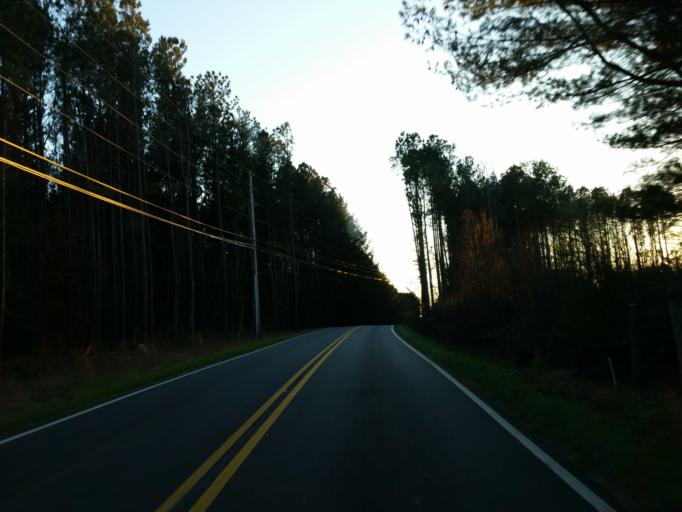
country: US
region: Georgia
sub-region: Cherokee County
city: Woodstock
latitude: 34.1215
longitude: -84.4500
